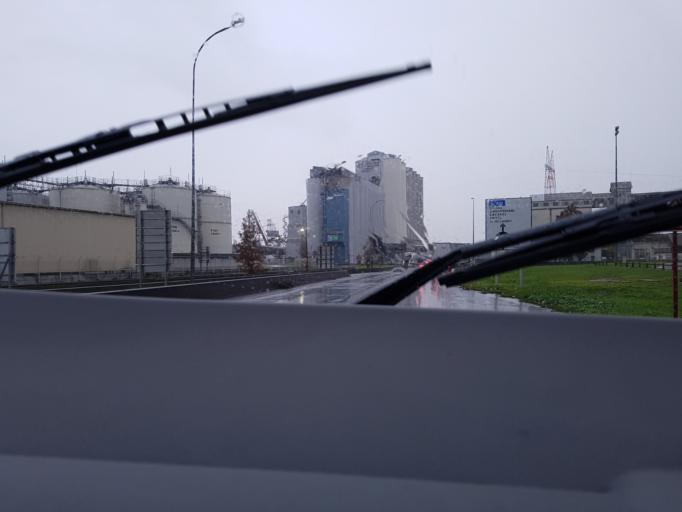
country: FR
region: Aquitaine
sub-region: Departement de la Gironde
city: Bassens
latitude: 44.9139
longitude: -0.5411
